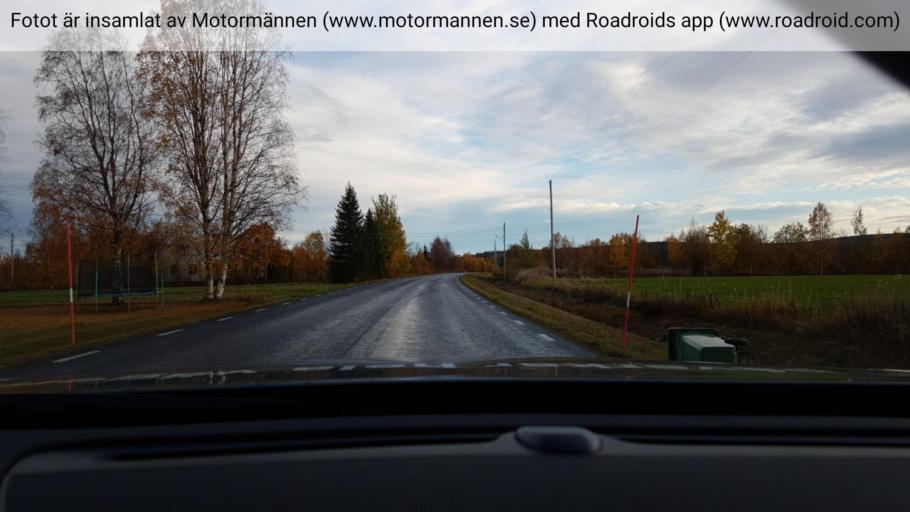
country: SE
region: Norrbotten
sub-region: Overkalix Kommun
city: OEverkalix
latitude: 66.9368
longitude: 22.7339
